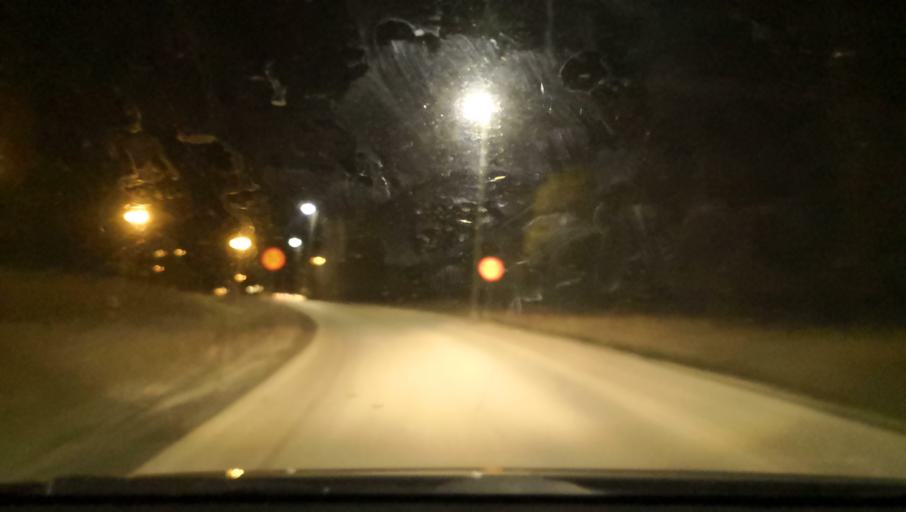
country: SE
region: Uppsala
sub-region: Uppsala Kommun
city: Uppsala
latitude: 59.8545
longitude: 17.5917
